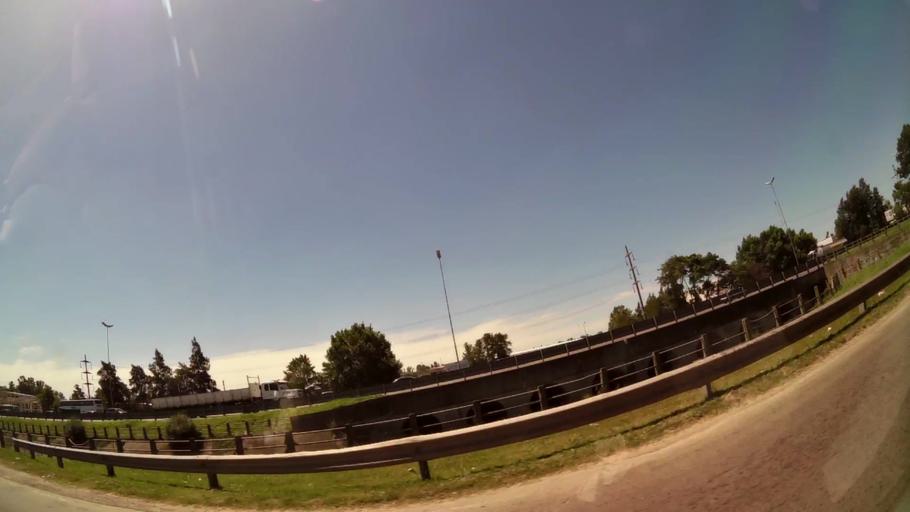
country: AR
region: Buenos Aires
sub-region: Partido de Tigre
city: Tigre
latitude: -34.4819
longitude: -58.6391
